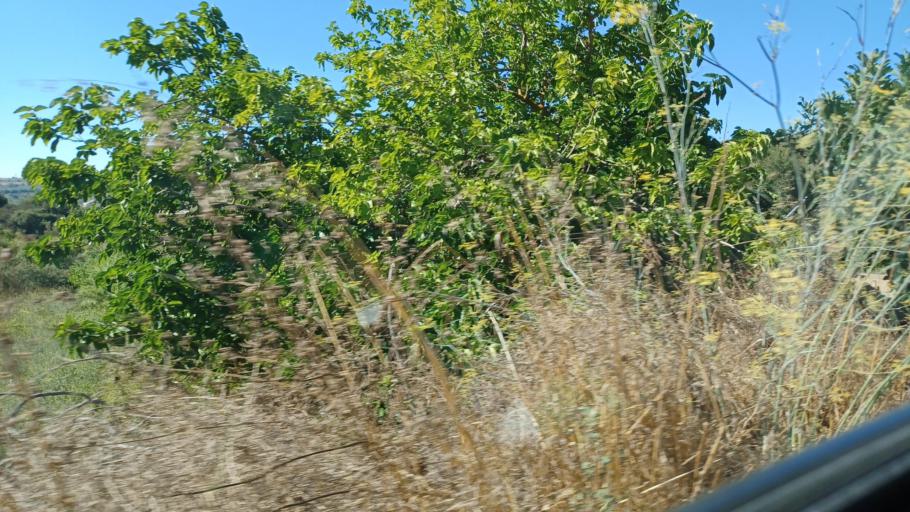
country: CY
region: Pafos
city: Mesogi
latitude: 34.8783
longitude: 32.5110
